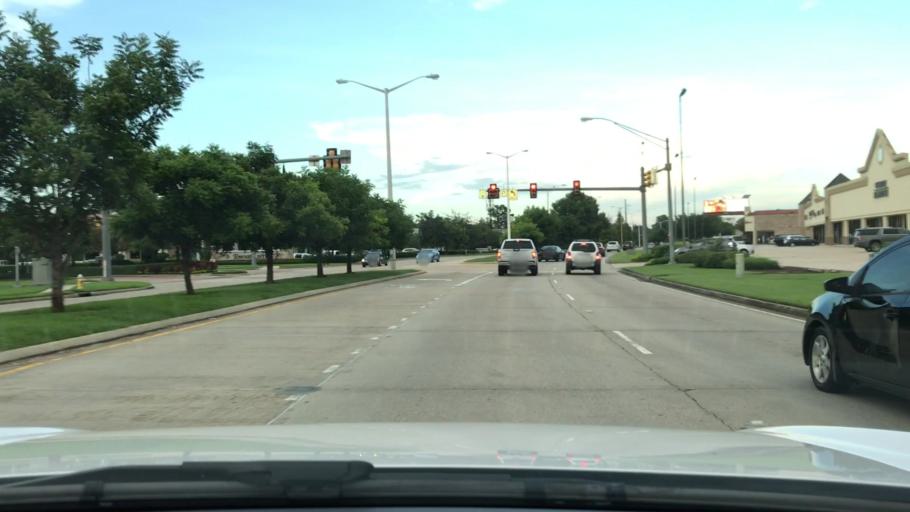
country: US
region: Louisiana
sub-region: East Baton Rouge Parish
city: Westminster
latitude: 30.4305
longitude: -91.1141
